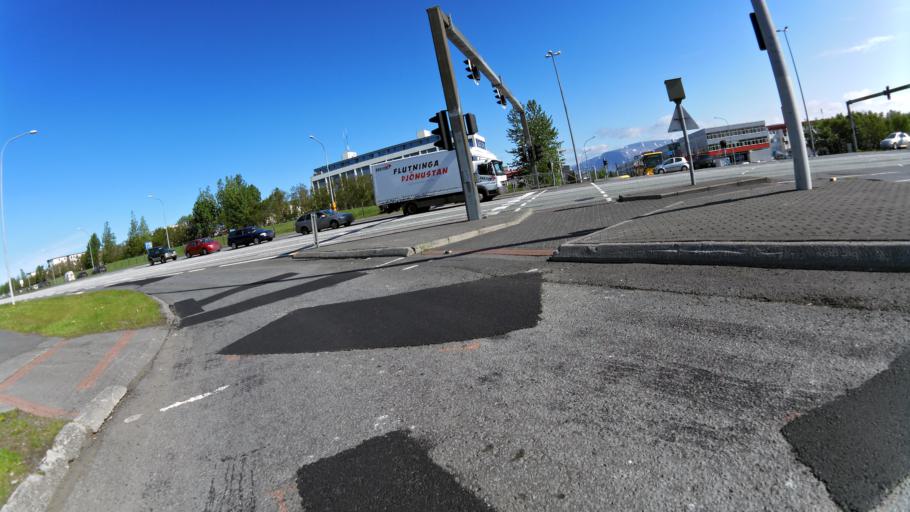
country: IS
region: Capital Region
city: Reykjavik
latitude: 64.1294
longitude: -21.8763
